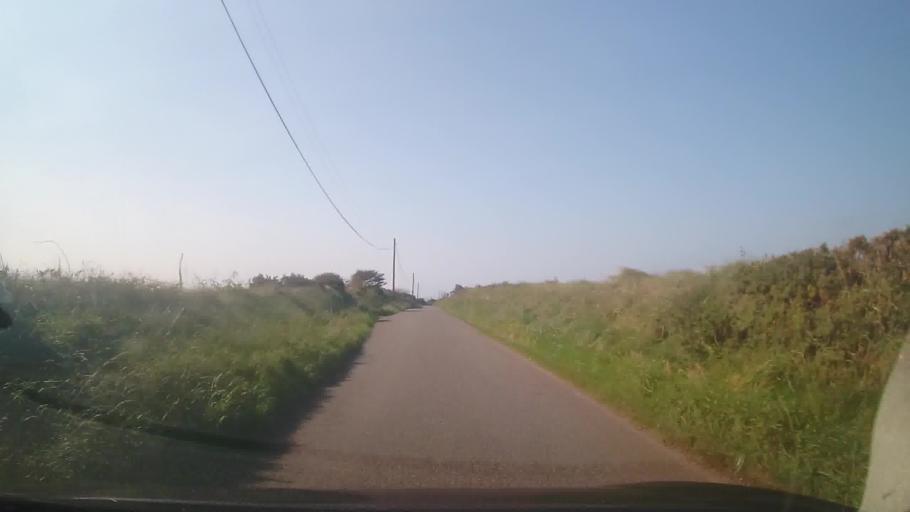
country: GB
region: Wales
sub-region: Pembrokeshire
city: Llanrhian
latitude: 51.9286
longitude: -5.1784
